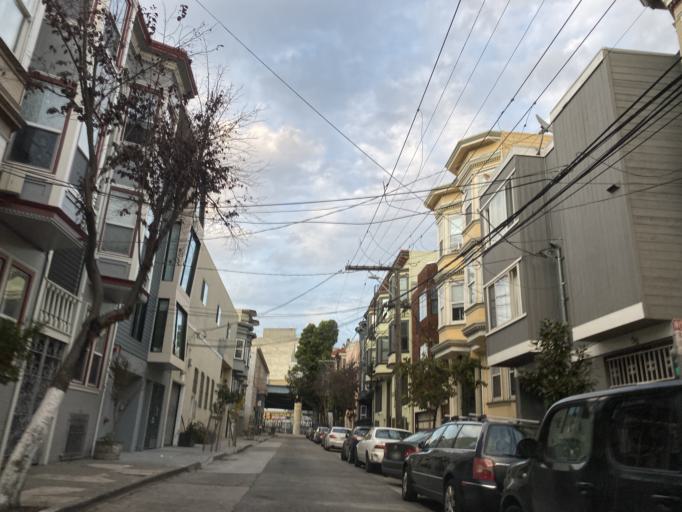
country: US
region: California
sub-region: San Francisco County
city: San Francisco
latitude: 37.7689
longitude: -122.4209
